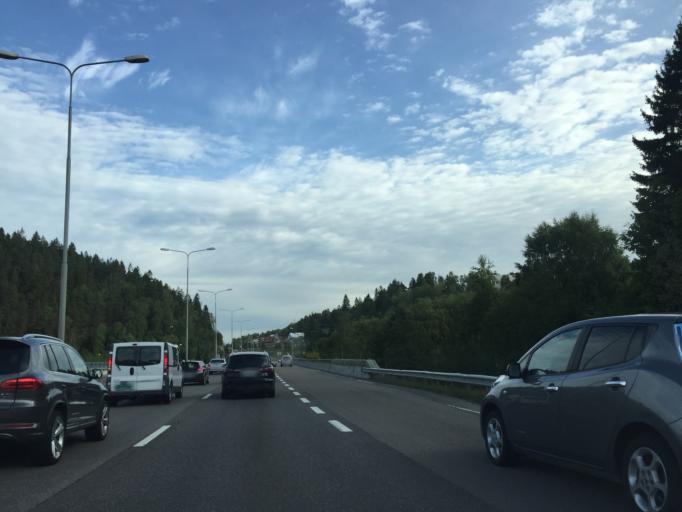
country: NO
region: Akershus
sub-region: Oppegard
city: Kolbotn
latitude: 59.8609
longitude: 10.8309
